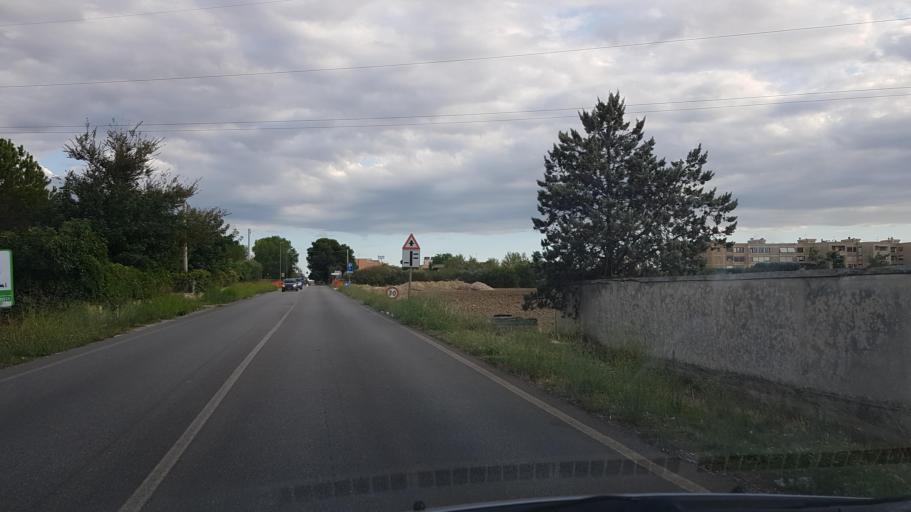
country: IT
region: Apulia
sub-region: Provincia di Brindisi
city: Francavilla Fontana
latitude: 40.5417
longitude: 17.5747
